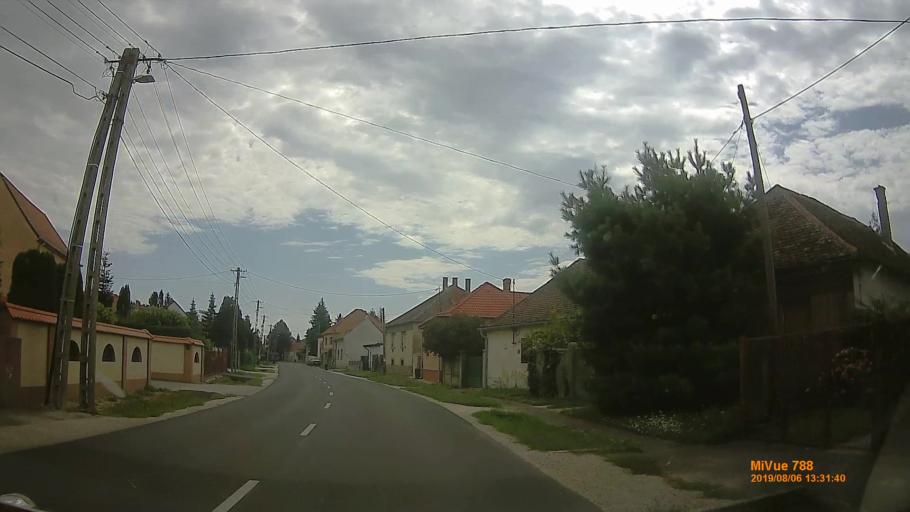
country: HU
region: Vas
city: Gencsapati
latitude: 47.2592
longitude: 16.6022
